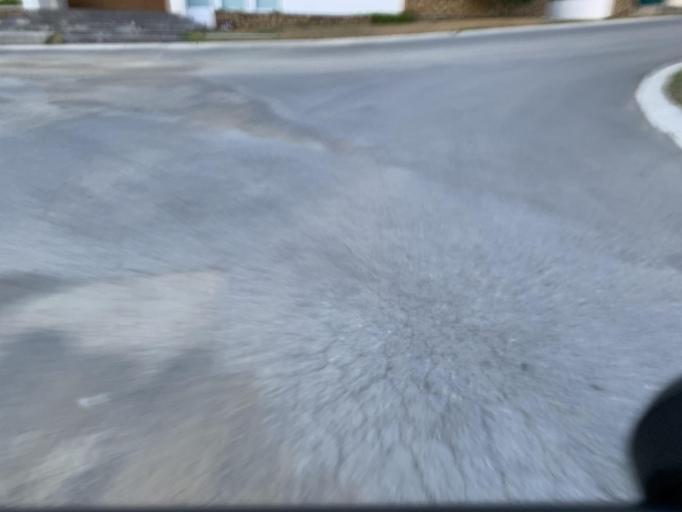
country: MX
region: Nuevo Leon
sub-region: Juarez
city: Bosques de San Pedro
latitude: 25.5227
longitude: -100.1924
